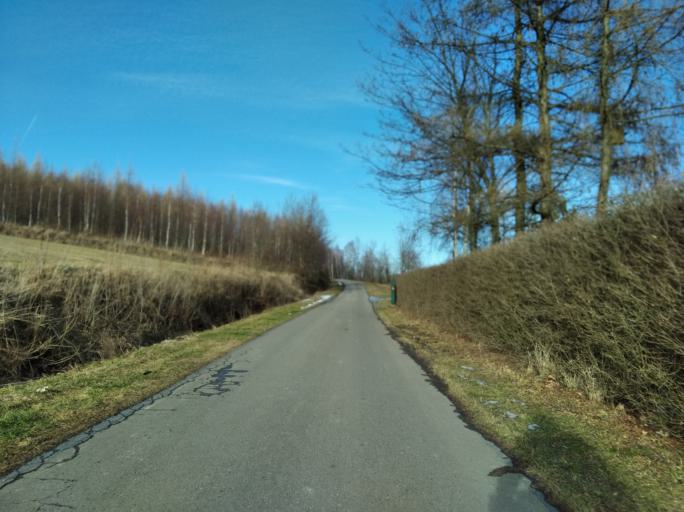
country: PL
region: Subcarpathian Voivodeship
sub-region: Powiat strzyzowski
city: Gwoznica Gorna
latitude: 49.8178
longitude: 21.9900
